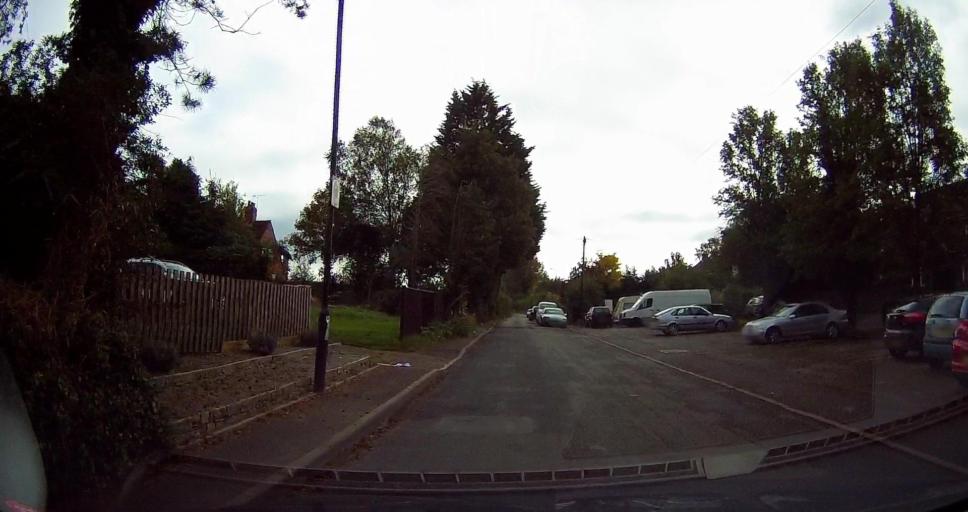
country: GB
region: England
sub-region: Kent
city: Hadlow
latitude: 51.2239
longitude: 0.3416
